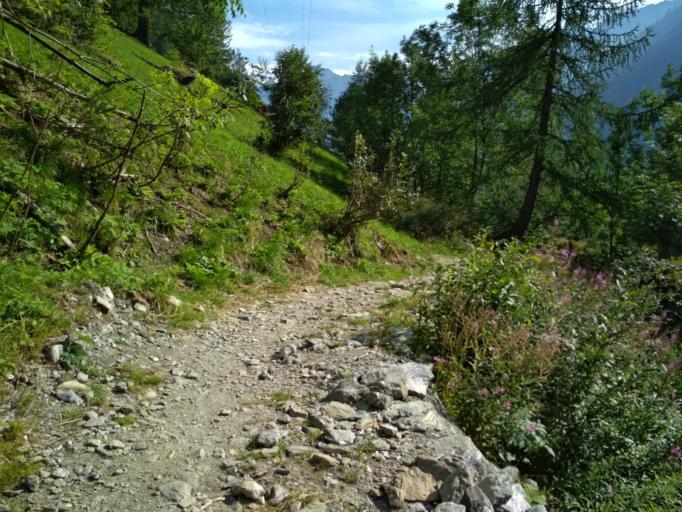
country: IT
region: Aosta Valley
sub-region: Valle d'Aosta
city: Gressoney-La-Trinite
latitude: 45.8056
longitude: 7.8271
